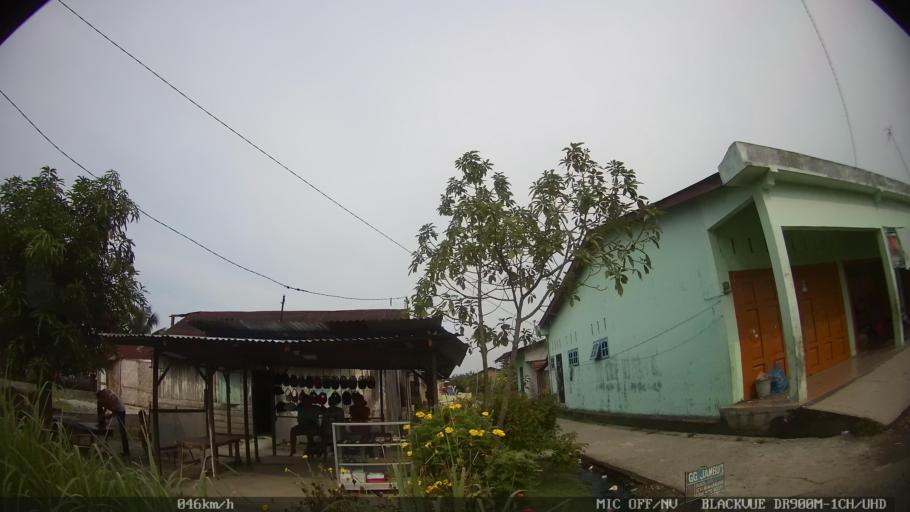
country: ID
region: North Sumatra
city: Medan
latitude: 3.5716
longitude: 98.7475
